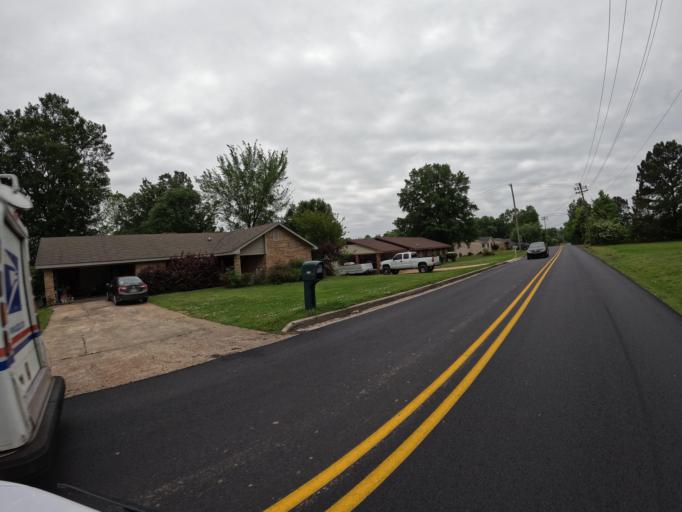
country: US
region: Mississippi
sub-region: Lee County
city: Tupelo
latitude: 34.2631
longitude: -88.7465
